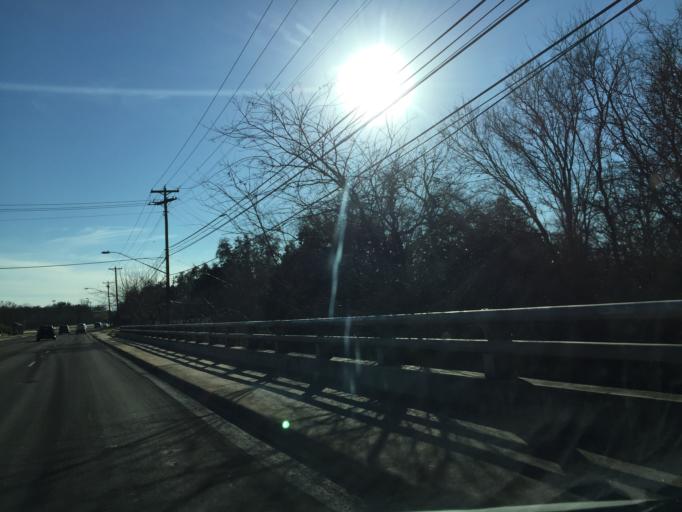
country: US
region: Texas
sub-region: Travis County
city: Austin
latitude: 30.2157
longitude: -97.7763
